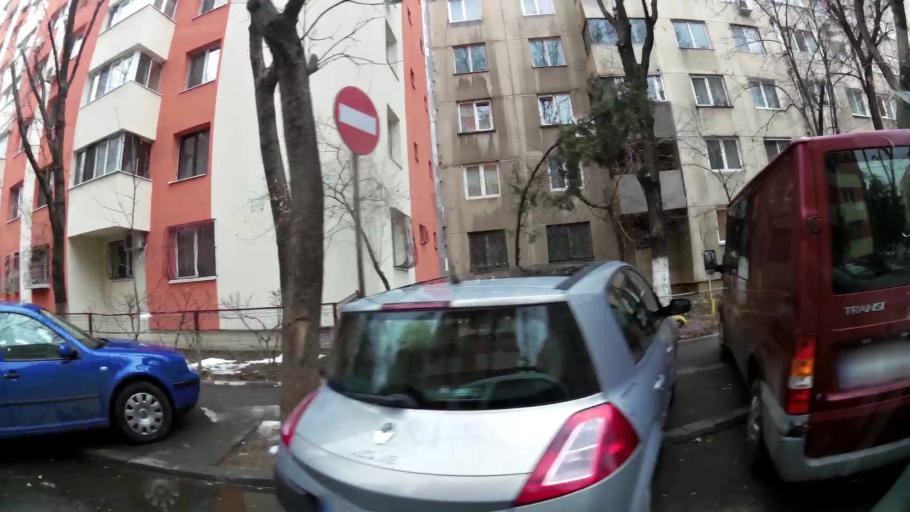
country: RO
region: Bucuresti
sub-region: Municipiul Bucuresti
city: Bucharest
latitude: 44.4585
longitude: 26.1268
